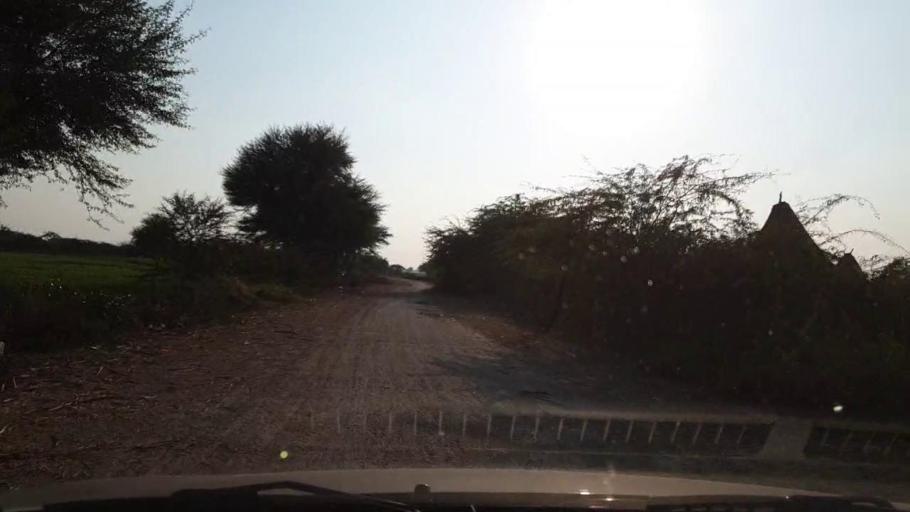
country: PK
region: Sindh
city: Jhol
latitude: 25.9302
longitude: 68.9090
